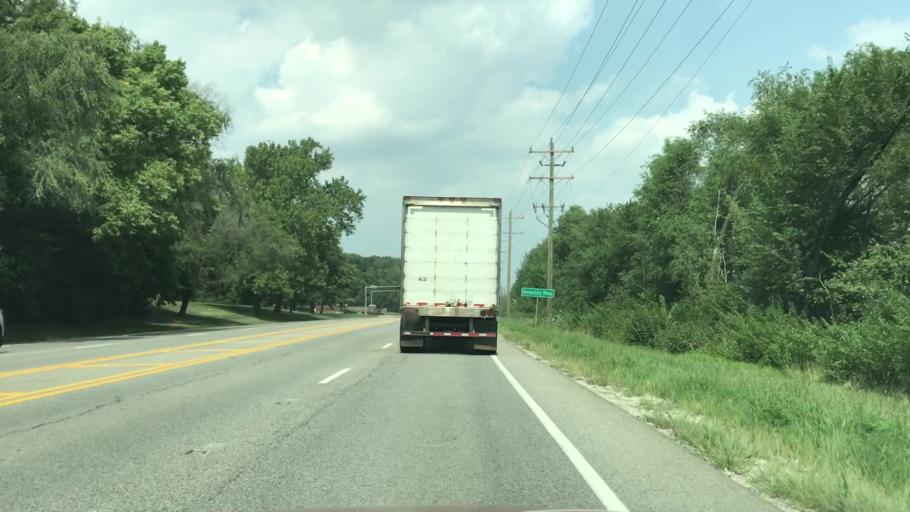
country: US
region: Illinois
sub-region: Will County
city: Lockport
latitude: 41.6035
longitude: -88.0754
